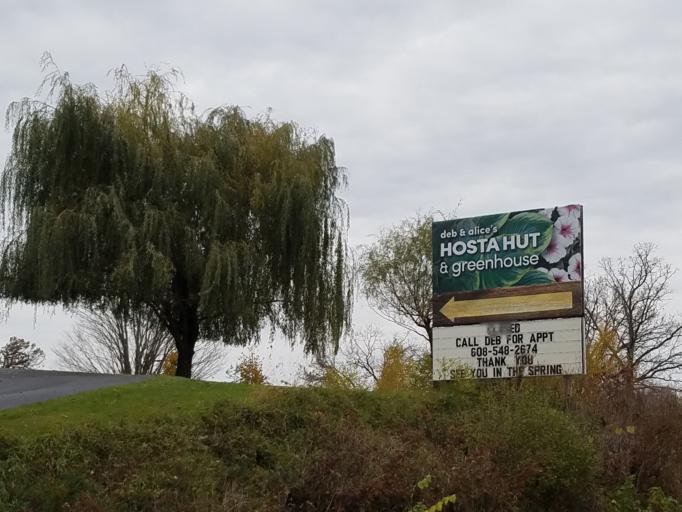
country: US
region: Wisconsin
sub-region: Vernon County
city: Hillsboro
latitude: 43.6608
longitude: -90.3314
